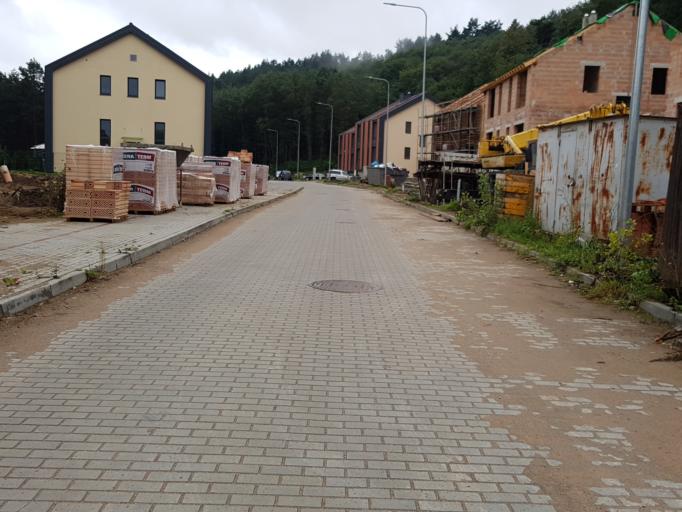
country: LT
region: Vilnius County
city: Lazdynai
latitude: 54.6654
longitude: 25.2232
